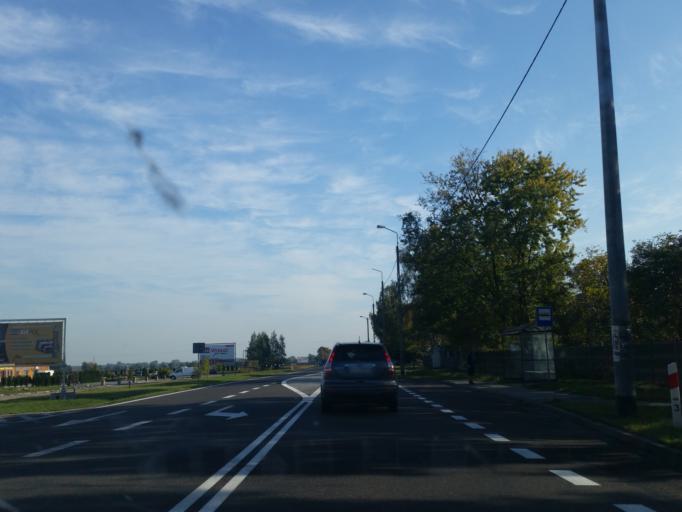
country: PL
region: Masovian Voivodeship
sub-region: Powiat plocki
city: Drobin
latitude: 52.7339
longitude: 19.9996
